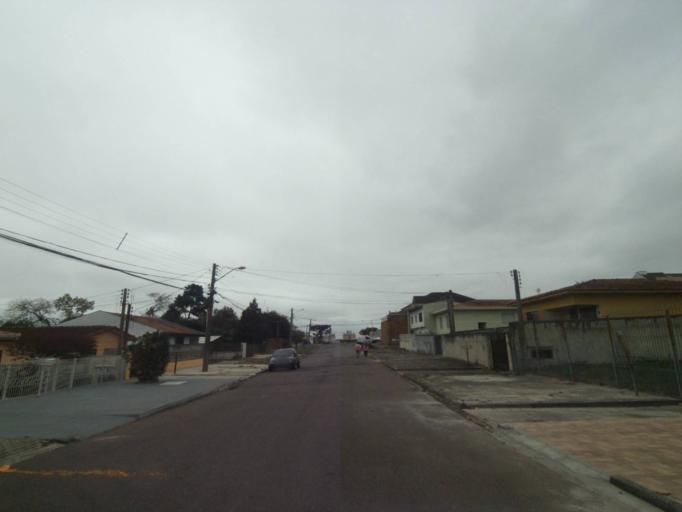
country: BR
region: Parana
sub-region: Curitiba
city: Curitiba
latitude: -25.4733
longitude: -49.2735
